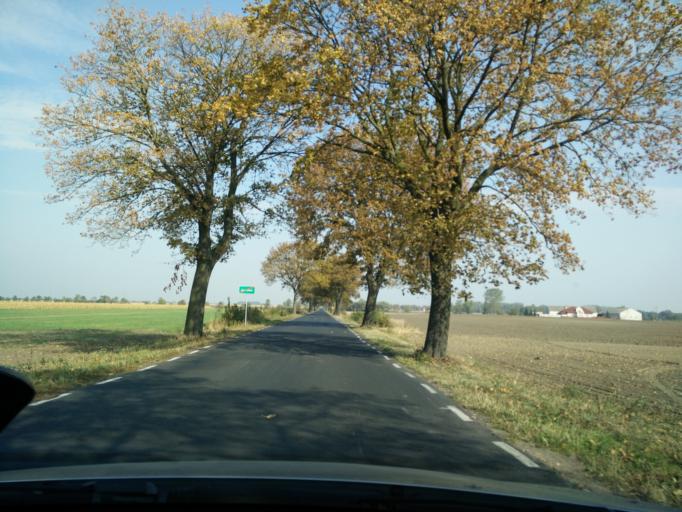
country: PL
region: Greater Poland Voivodeship
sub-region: Powiat sredzki
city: Sroda Wielkopolska
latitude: 52.2525
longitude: 17.2979
